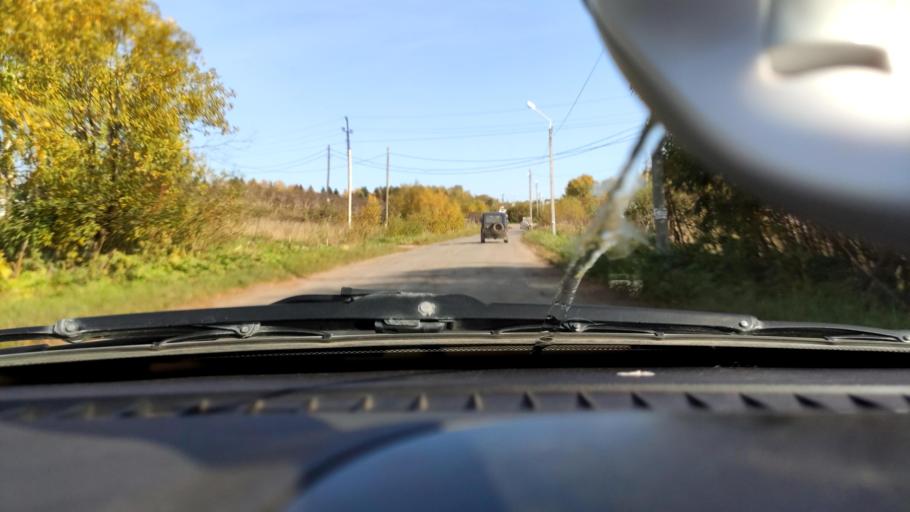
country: RU
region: Perm
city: Overyata
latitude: 58.0768
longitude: 55.8878
